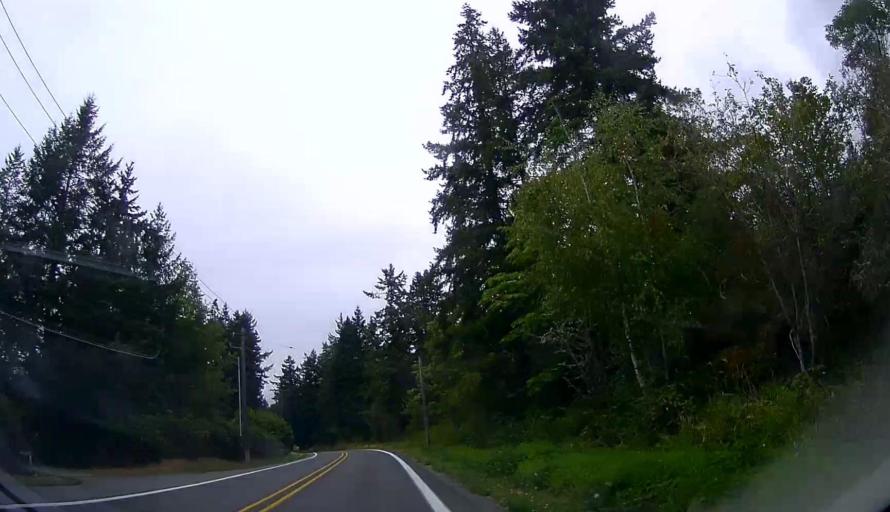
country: US
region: Washington
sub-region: Snohomish County
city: Warm Beach
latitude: 48.1509
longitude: -122.3603
